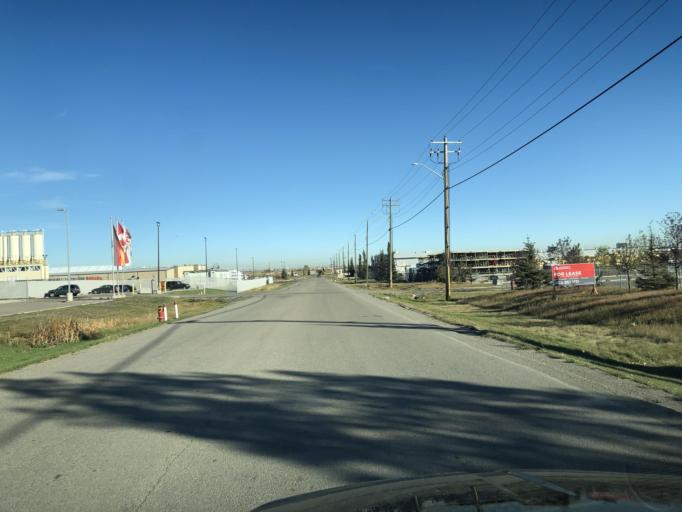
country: CA
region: Alberta
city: Chestermere
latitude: 50.9666
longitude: -113.9026
